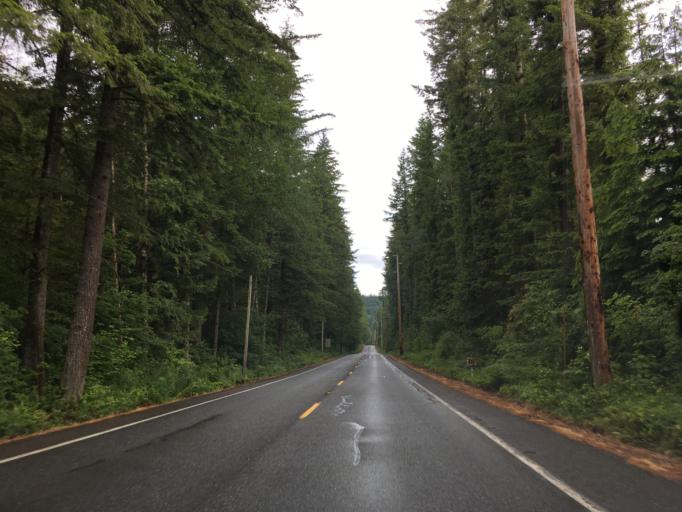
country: US
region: Washington
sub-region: Whatcom County
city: Peaceful Valley
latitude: 48.9610
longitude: -122.1596
